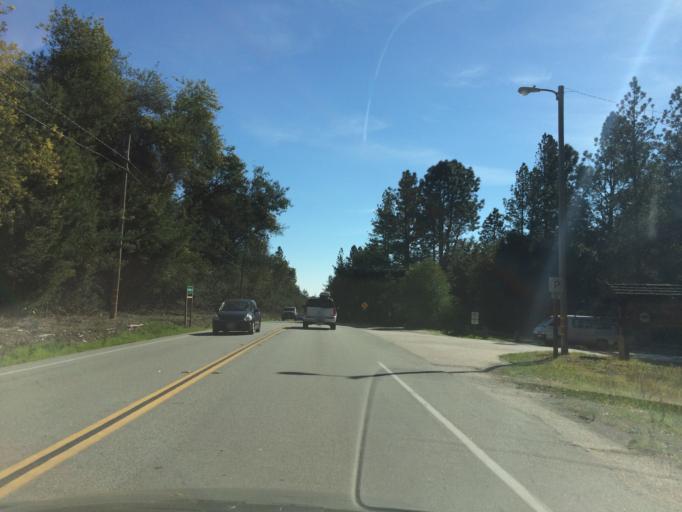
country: US
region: California
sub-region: Santa Cruz County
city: Mount Hermon
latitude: 37.0303
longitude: -122.0403
